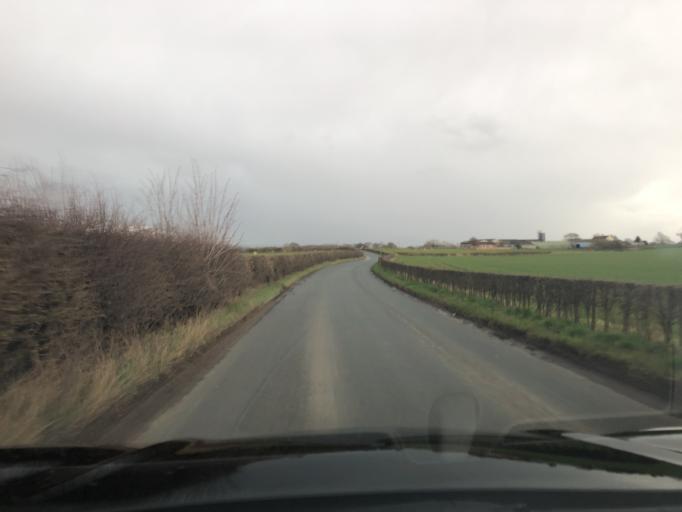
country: GB
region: England
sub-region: North Yorkshire
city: Northallerton
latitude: 54.3436
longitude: -1.4616
